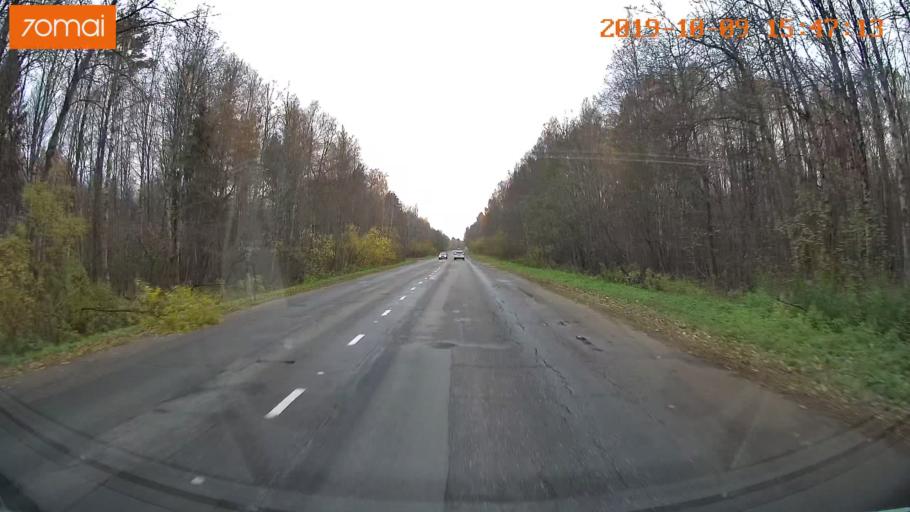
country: RU
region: Kostroma
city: Oktyabr'skiy
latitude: 57.8190
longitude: 41.0318
